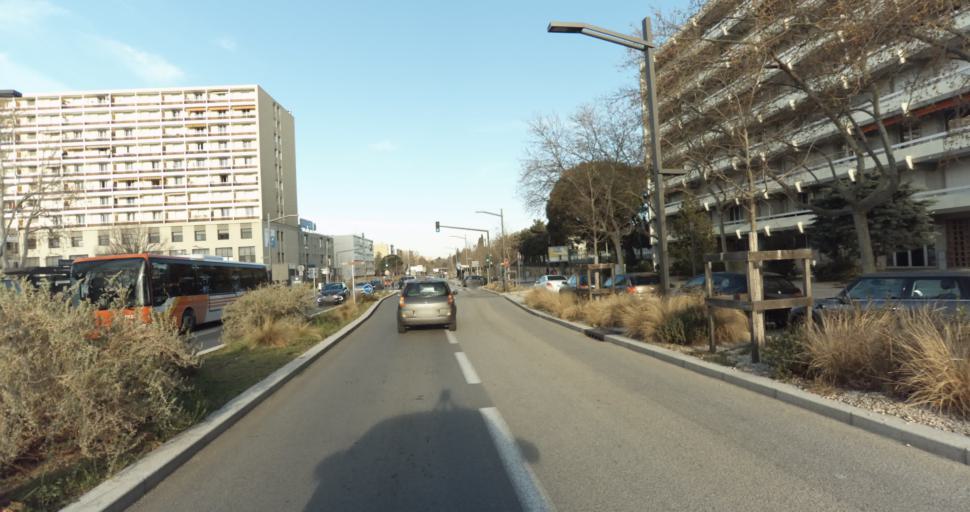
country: FR
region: Provence-Alpes-Cote d'Azur
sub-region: Departement des Bouches-du-Rhone
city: Aix-en-Provence
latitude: 43.5240
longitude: 5.4342
